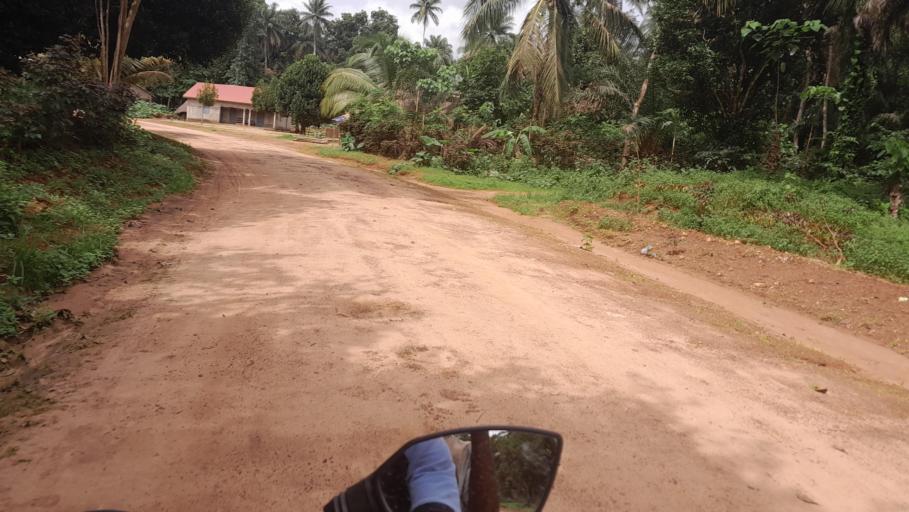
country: GN
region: Boke
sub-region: Boffa
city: Boffa
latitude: 10.0862
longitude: -13.8649
